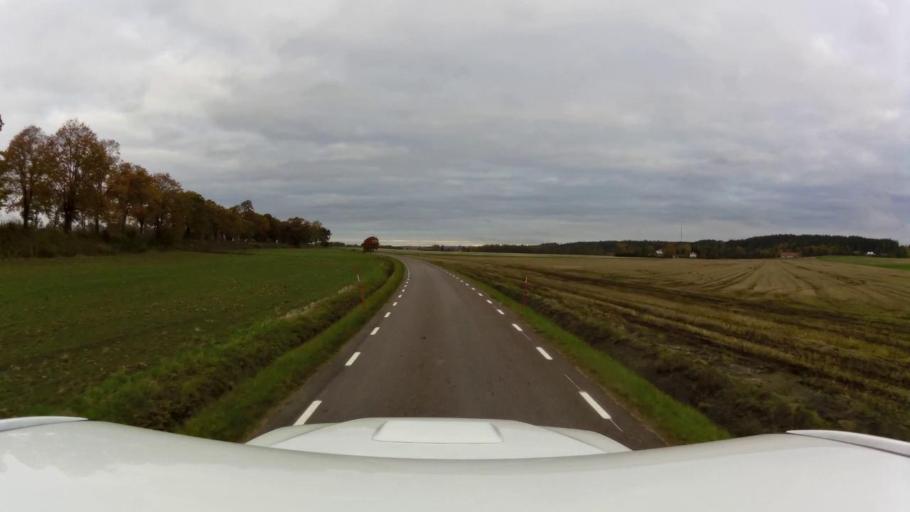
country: SE
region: OEstergoetland
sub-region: Linkopings Kommun
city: Ljungsbro
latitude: 58.5295
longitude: 15.4205
